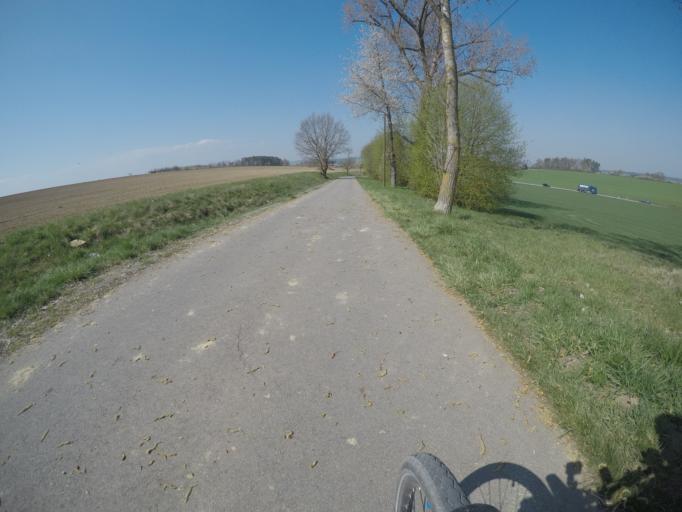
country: DE
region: Baden-Wuerttemberg
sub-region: Regierungsbezirk Stuttgart
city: Renningen
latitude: 48.7480
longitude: 8.9111
